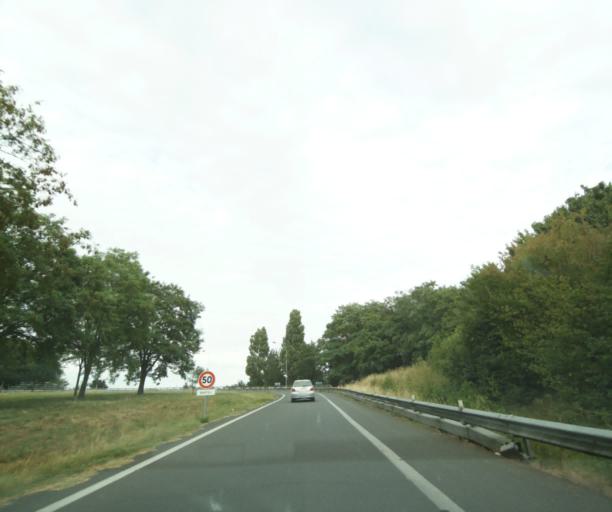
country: FR
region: Poitou-Charentes
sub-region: Departement de la Charente-Maritime
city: Sainte-Soulle
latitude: 46.2004
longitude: -1.0285
